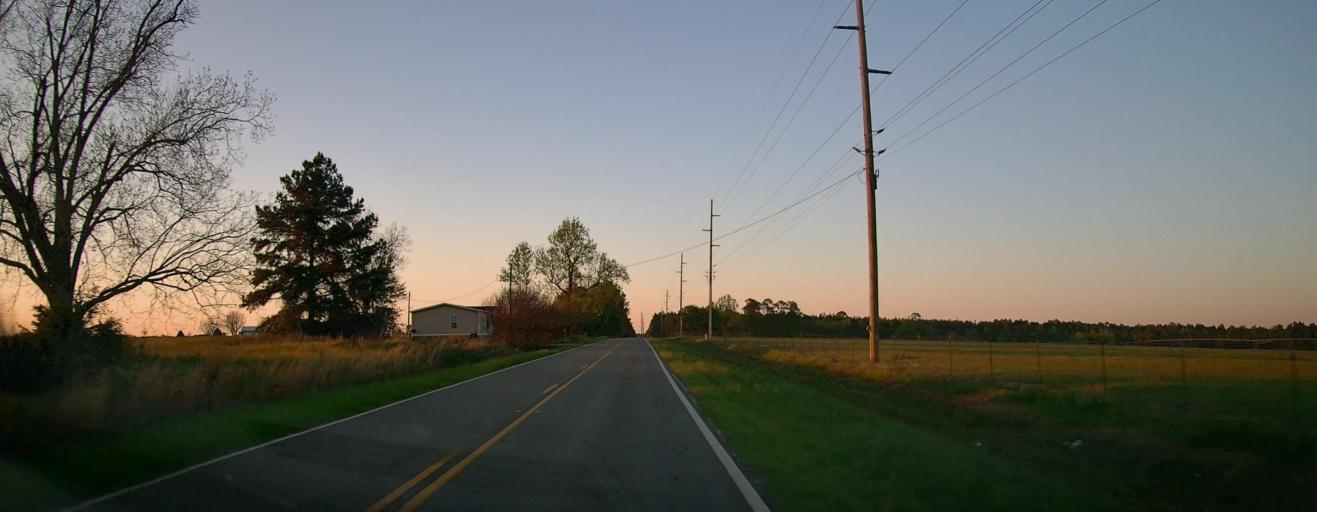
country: US
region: Georgia
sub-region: Ben Hill County
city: Fitzgerald
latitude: 31.7652
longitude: -83.3550
